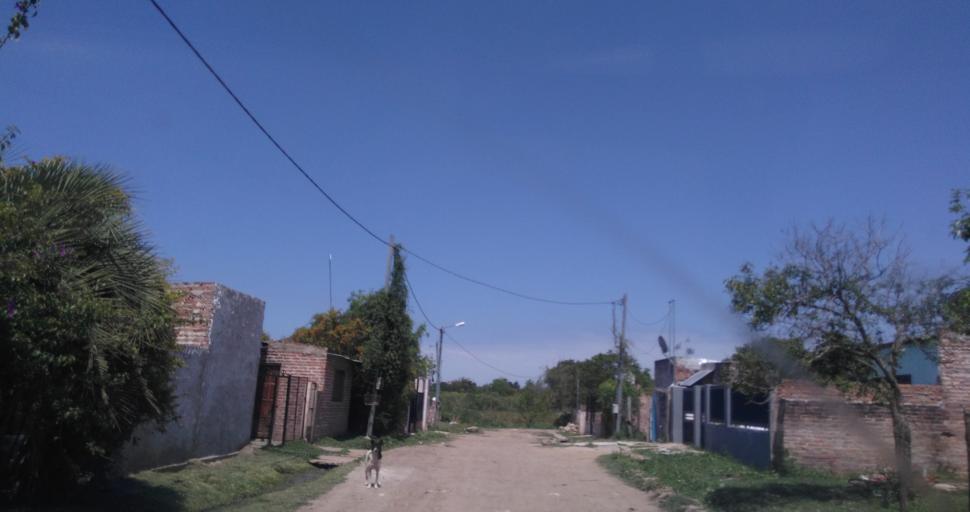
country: AR
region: Chaco
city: Resistencia
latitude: -27.4195
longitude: -58.9812
